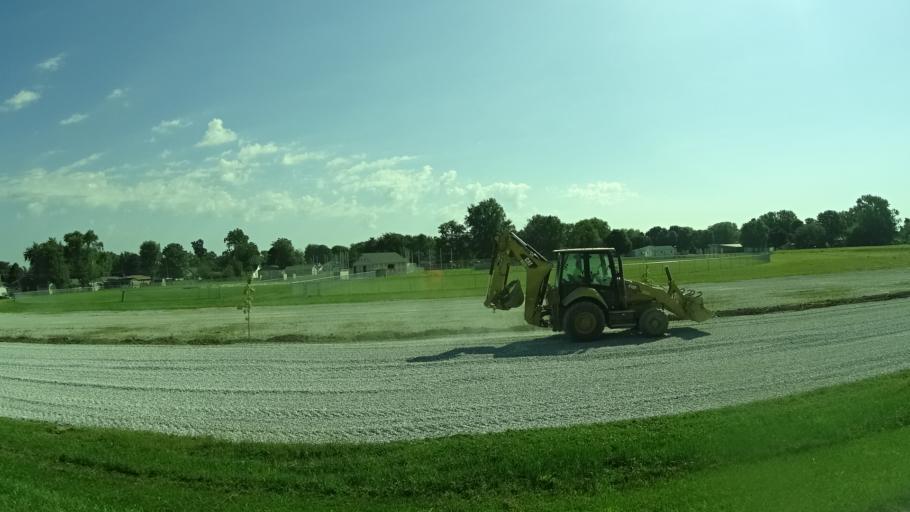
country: US
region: Indiana
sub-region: Madison County
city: Lapel
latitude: 40.0641
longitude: -85.8535
